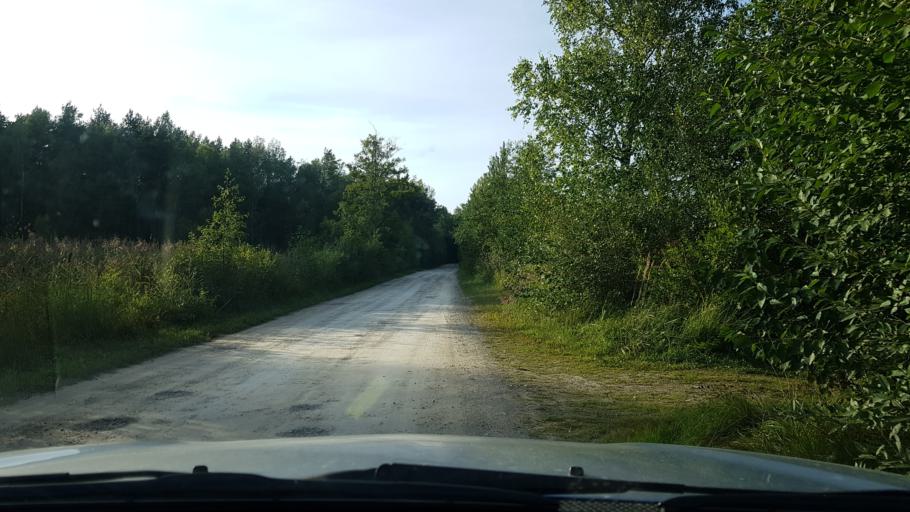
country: EE
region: Ida-Virumaa
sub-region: Sillamaee linn
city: Sillamae
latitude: 59.2593
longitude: 27.9248
